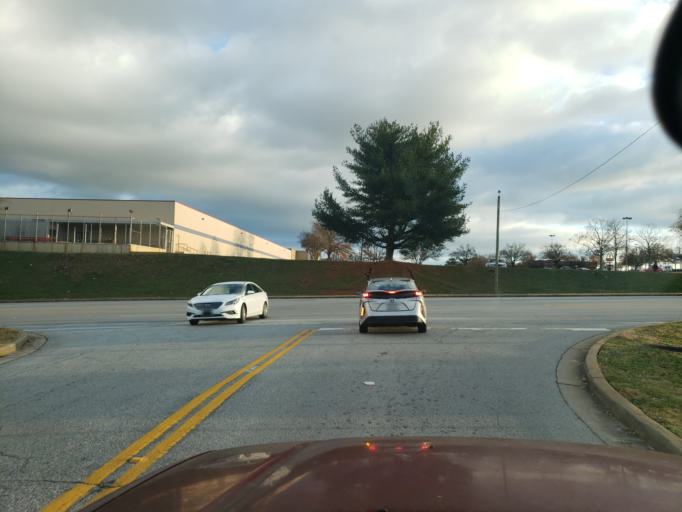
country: US
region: South Carolina
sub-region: Greenville County
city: Greenville
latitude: 34.8312
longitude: -82.3467
